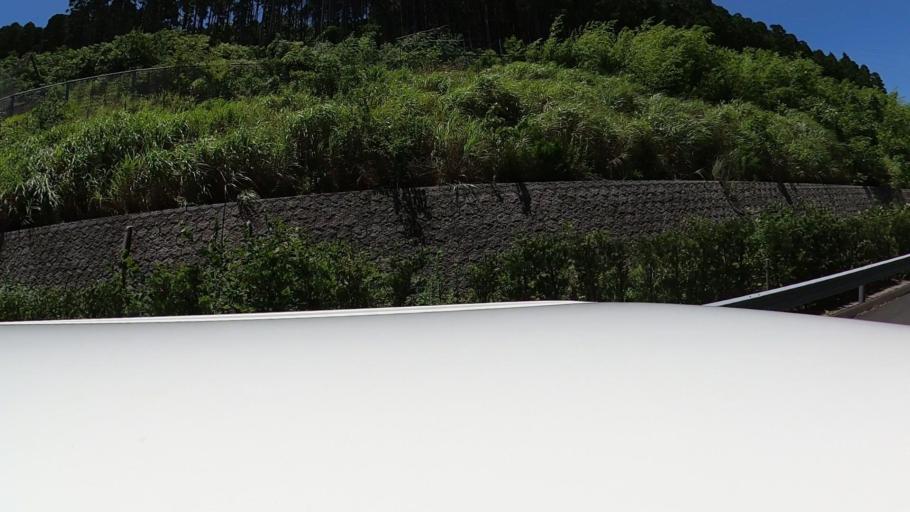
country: JP
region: Miyazaki
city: Nobeoka
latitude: 32.3934
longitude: 131.6216
